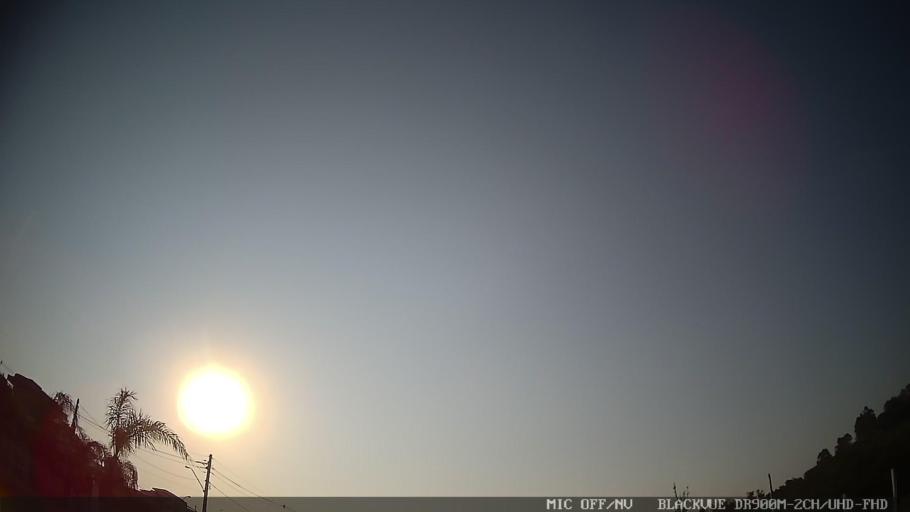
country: BR
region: Sao Paulo
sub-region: Itatiba
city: Itatiba
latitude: -23.0299
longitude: -46.8323
